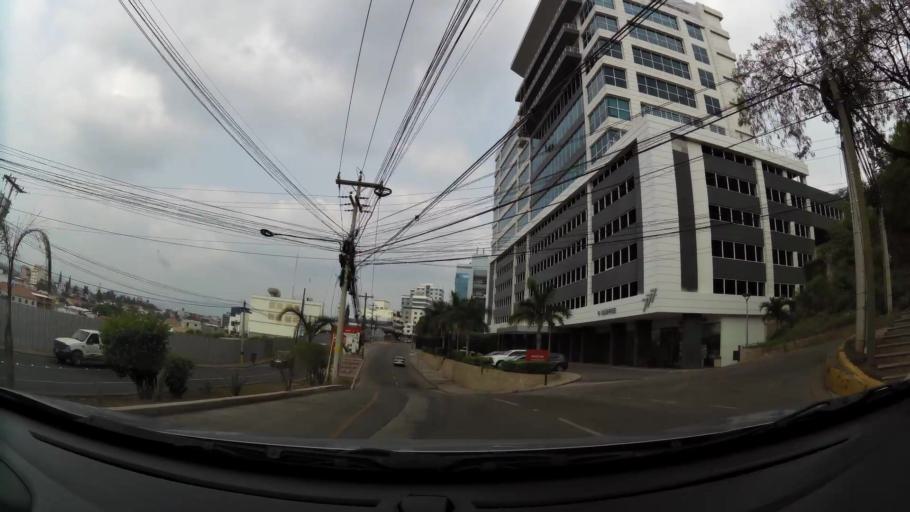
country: HN
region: Francisco Morazan
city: Tegucigalpa
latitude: 14.0896
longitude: -87.1744
